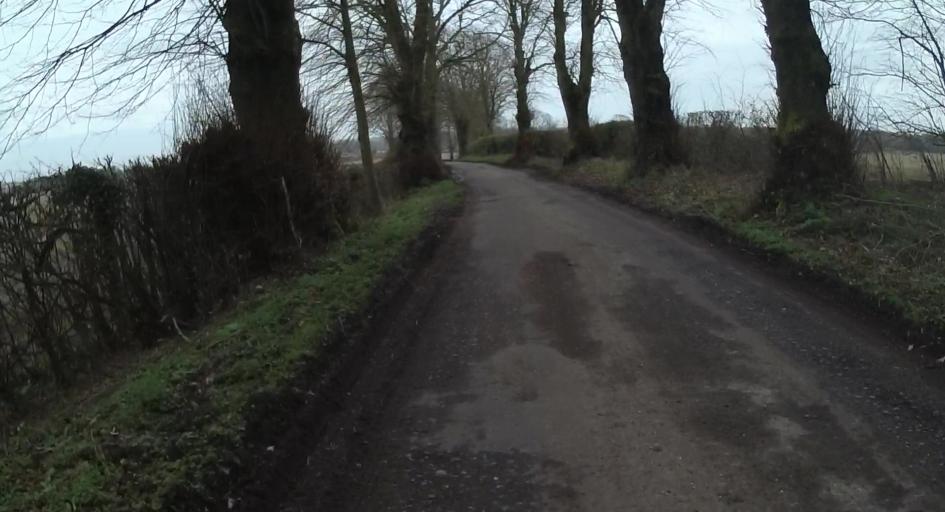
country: GB
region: England
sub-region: Hampshire
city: Overton
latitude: 51.2623
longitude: -1.1840
